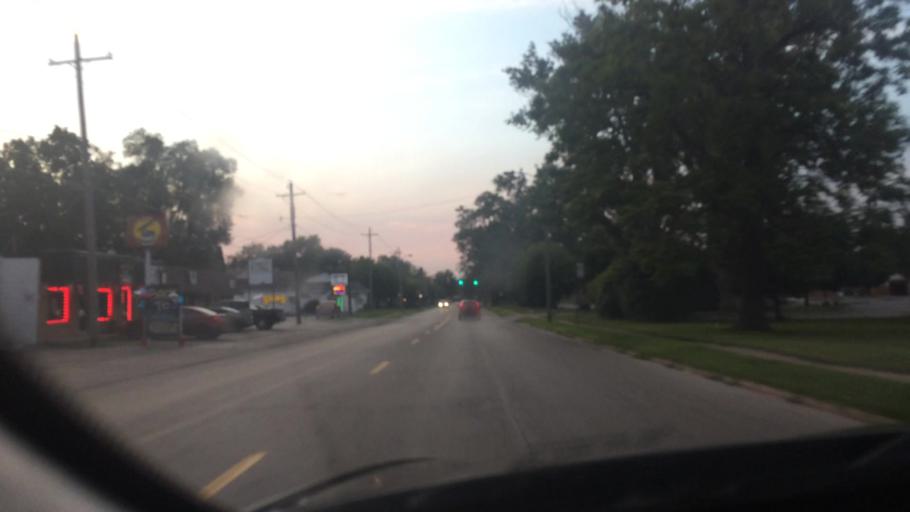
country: US
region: Michigan
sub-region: Monroe County
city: Lambertville
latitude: 41.7167
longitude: -83.6163
